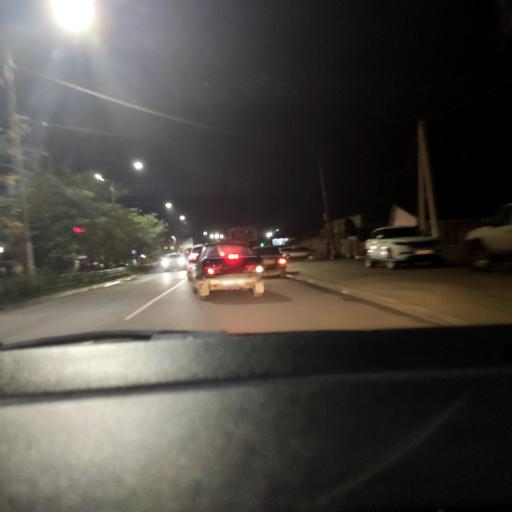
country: RU
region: Voronezj
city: Voronezh
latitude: 51.6483
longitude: 39.1850
